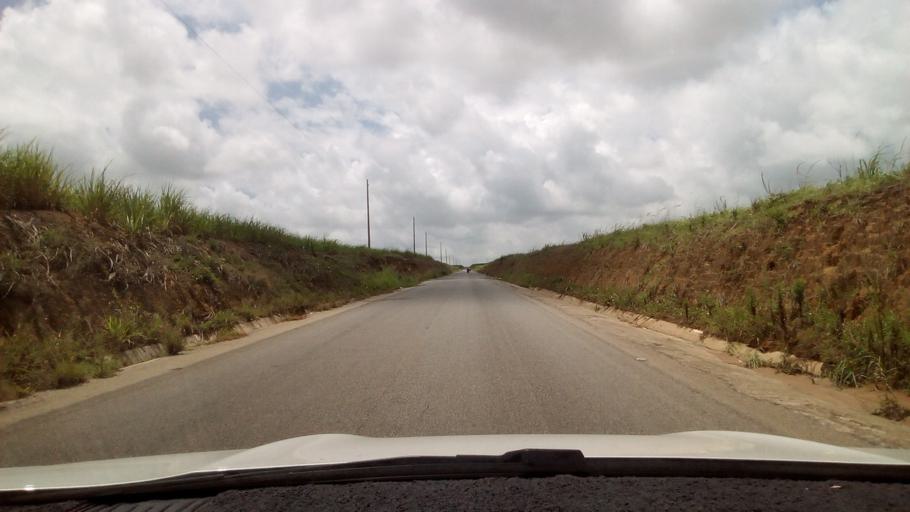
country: BR
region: Paraiba
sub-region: Caapora
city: Caapora
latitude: -7.4898
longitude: -34.9185
